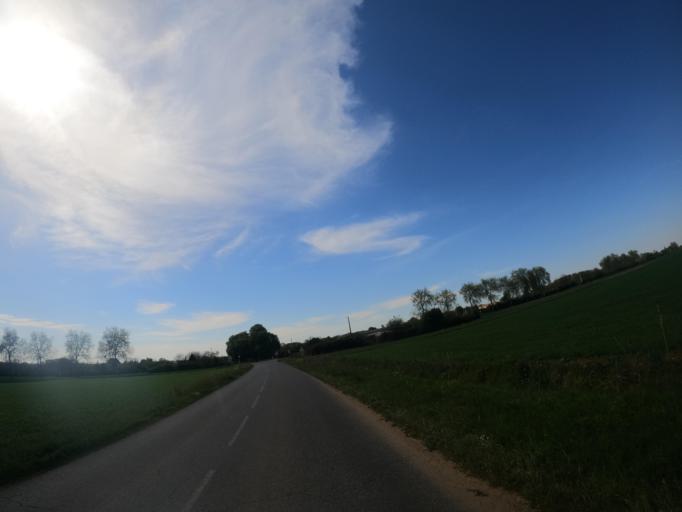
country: FR
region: Poitou-Charentes
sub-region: Departement des Deux-Sevres
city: Saint-Varent
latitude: 46.9021
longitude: -0.1930
